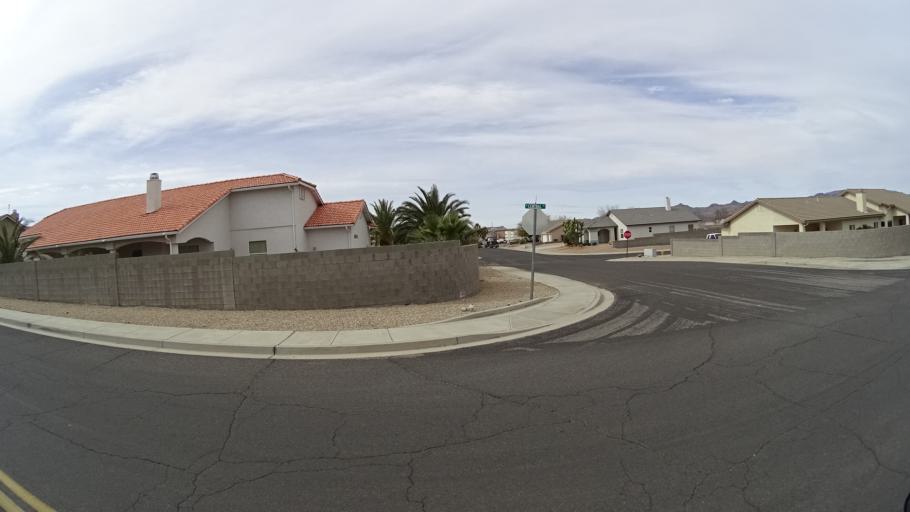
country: US
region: Arizona
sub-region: Mohave County
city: Kingman
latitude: 35.1933
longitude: -114.0027
